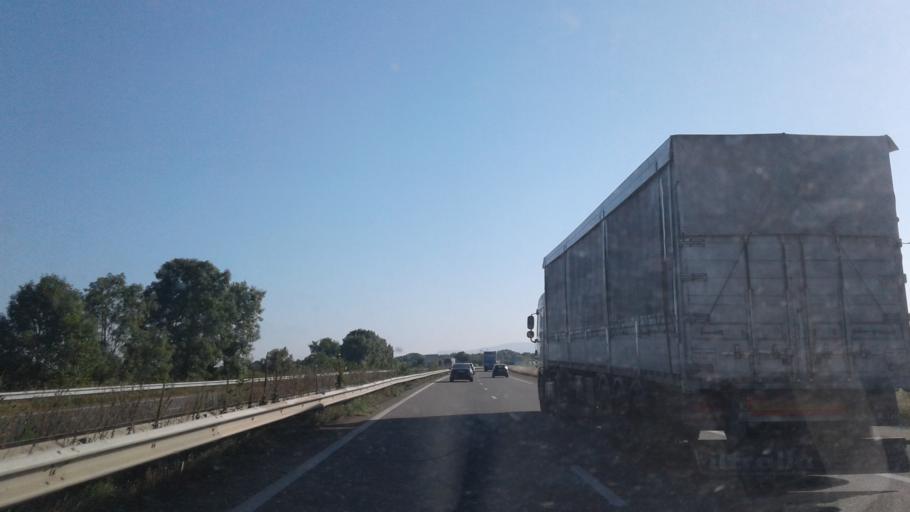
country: FR
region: Rhone-Alpes
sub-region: Departement de l'Ain
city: Meximieux
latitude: 45.8991
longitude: 5.2238
